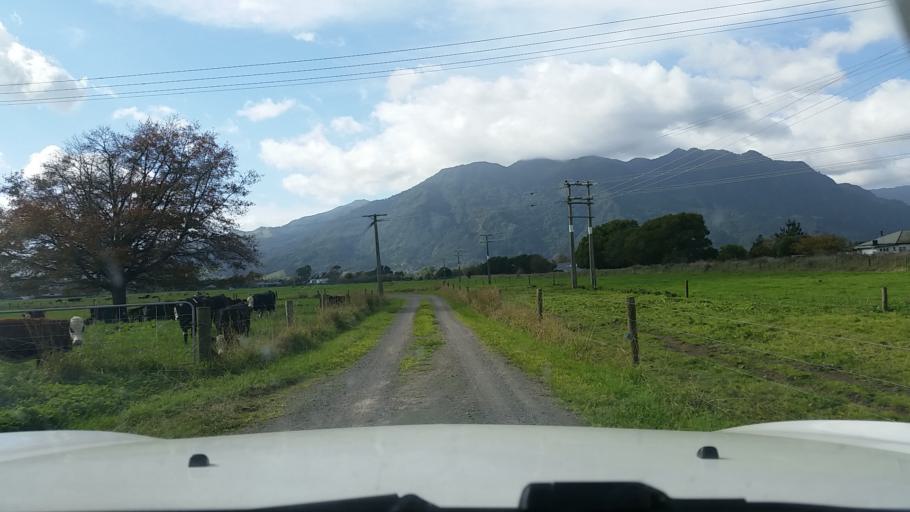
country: NZ
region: Waikato
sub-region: Hauraki District
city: Paeroa
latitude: -37.5600
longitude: 175.6853
